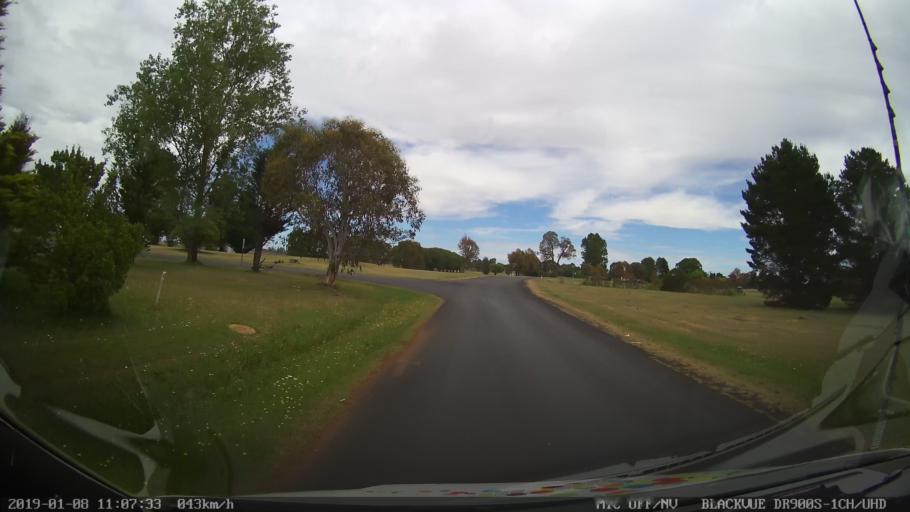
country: AU
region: New South Wales
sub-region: Guyra
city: Guyra
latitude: -30.2167
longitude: 151.6644
